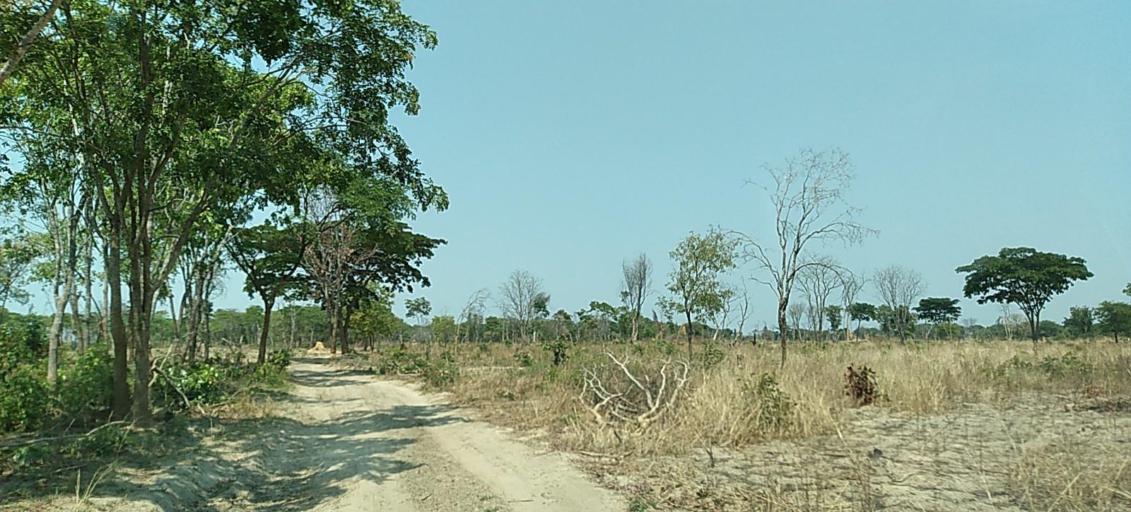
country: ZM
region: Copperbelt
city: Mpongwe
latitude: -13.8688
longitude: 28.0522
